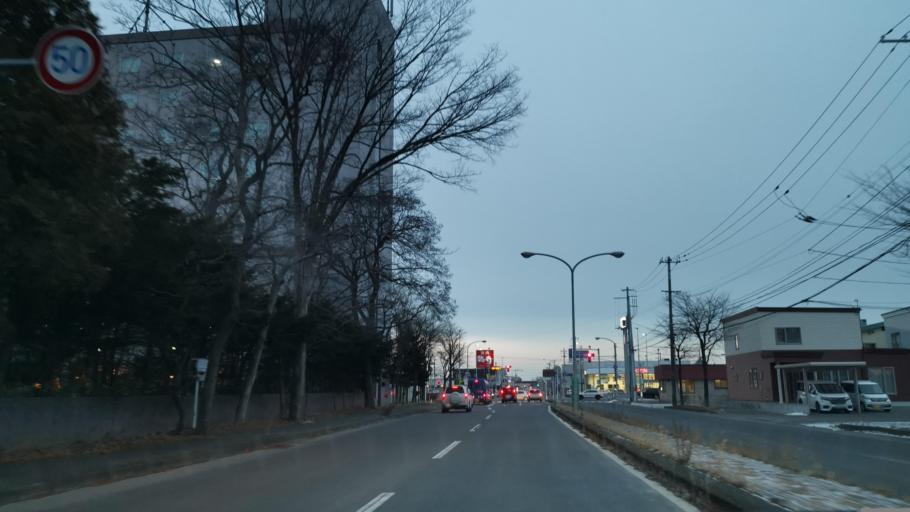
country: JP
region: Hokkaido
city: Chitose
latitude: 42.8165
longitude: 141.6473
